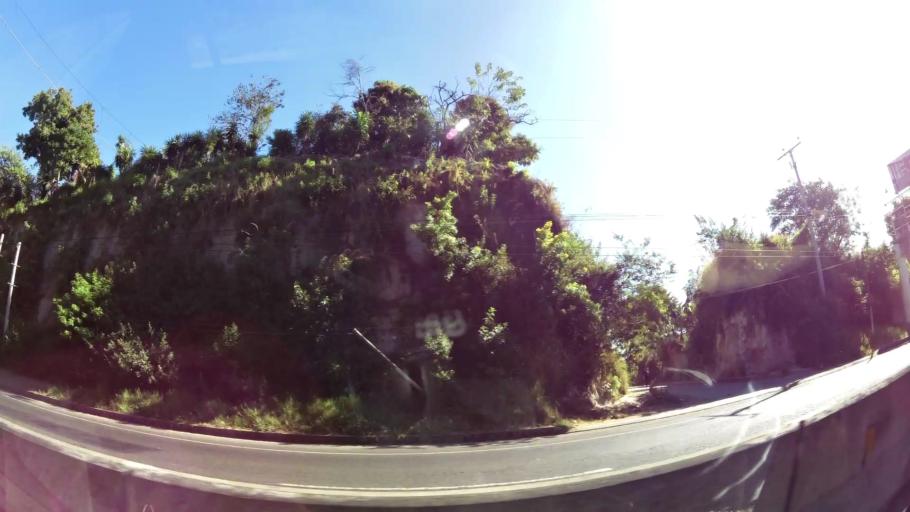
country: SV
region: Santa Ana
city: Coatepeque
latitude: 13.9302
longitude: -89.5221
